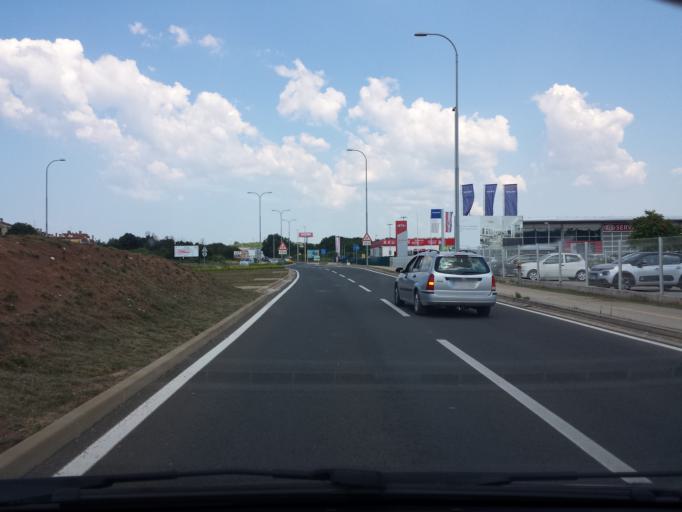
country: HR
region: Istarska
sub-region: Grad Pula
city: Pula
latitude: 44.8824
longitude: 13.8630
